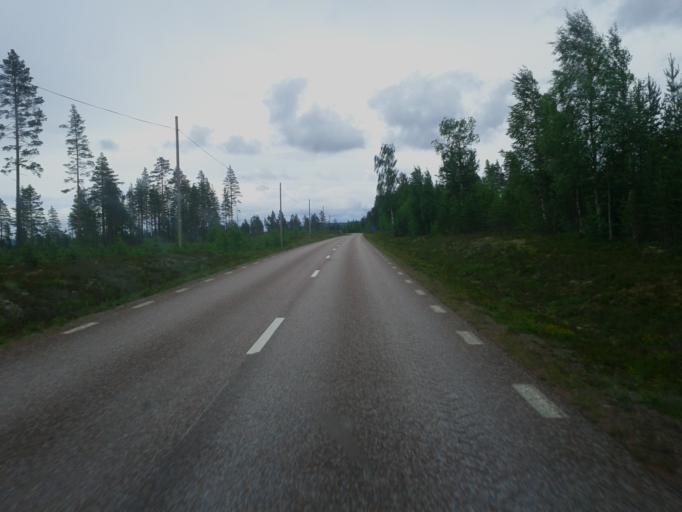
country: NO
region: Hedmark
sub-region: Trysil
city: Innbygda
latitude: 61.6949
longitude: 13.0512
